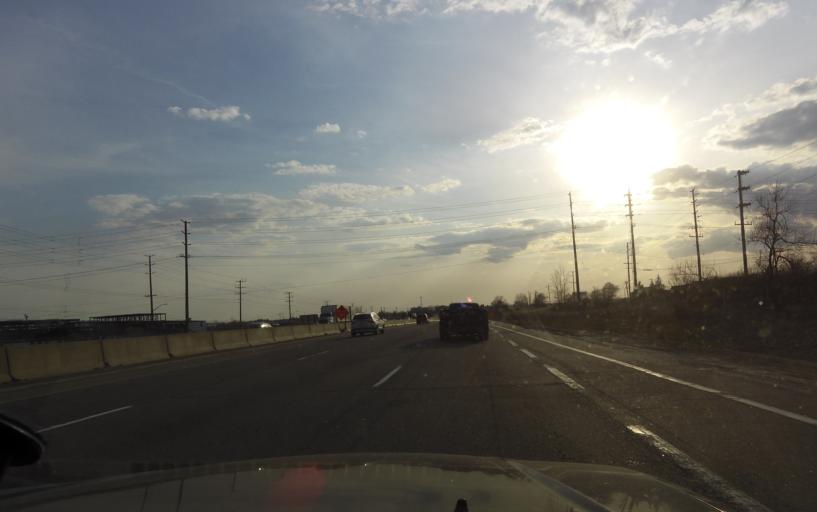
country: CA
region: Ontario
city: Oshawa
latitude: 43.8674
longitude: -78.9138
